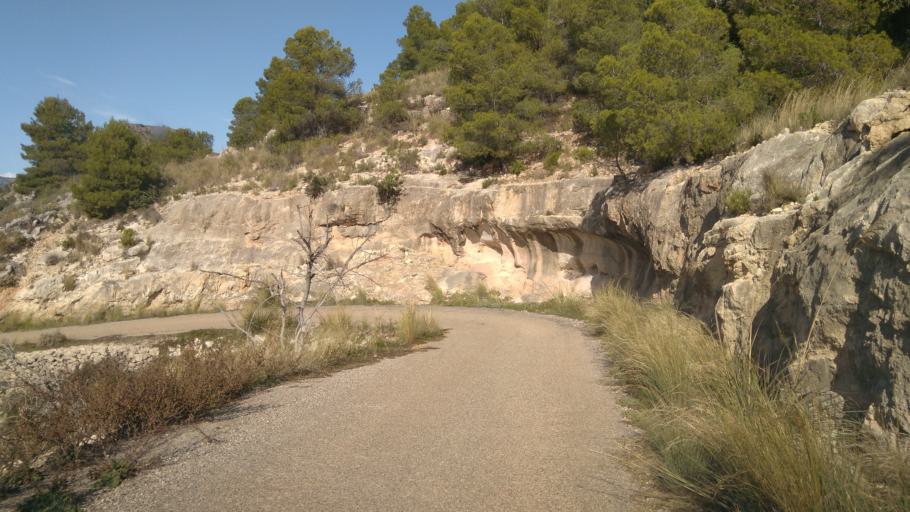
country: ES
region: Valencia
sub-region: Provincia de Valencia
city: Sumacarcer
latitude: 39.1526
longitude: -0.6556
